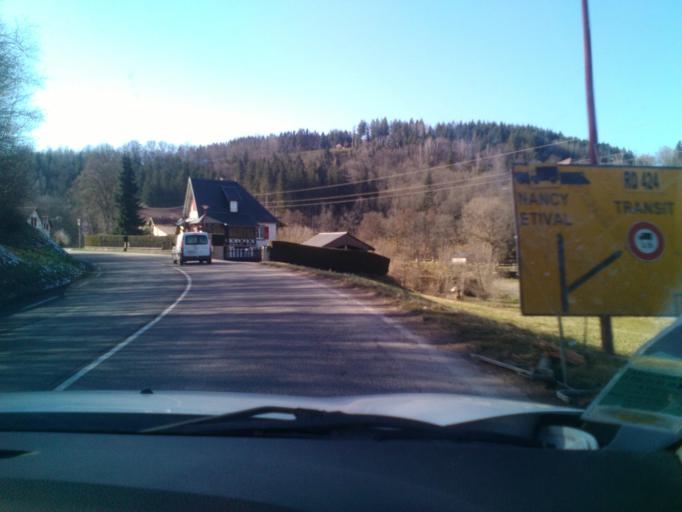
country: FR
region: Alsace
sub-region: Departement du Bas-Rhin
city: Rothau
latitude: 48.4045
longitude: 7.1576
